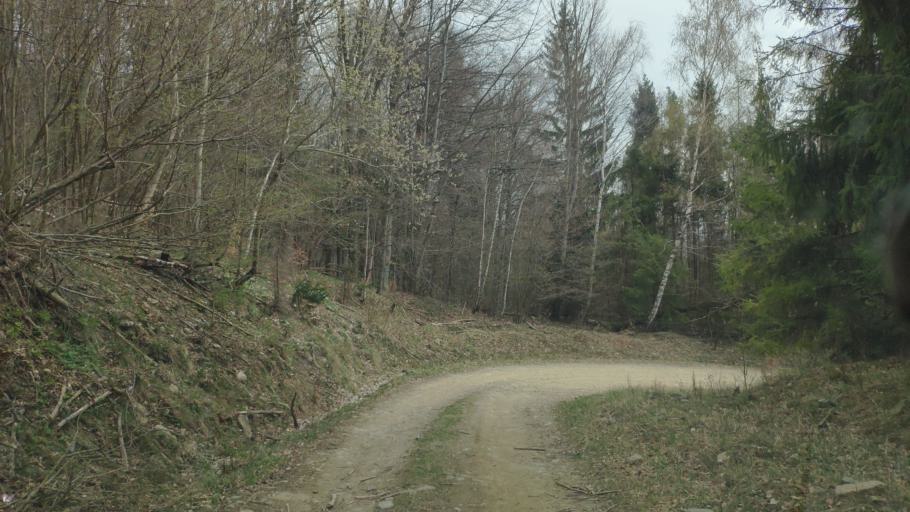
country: SK
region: Kosicky
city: Moldava nad Bodvou
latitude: 48.7427
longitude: 21.0366
